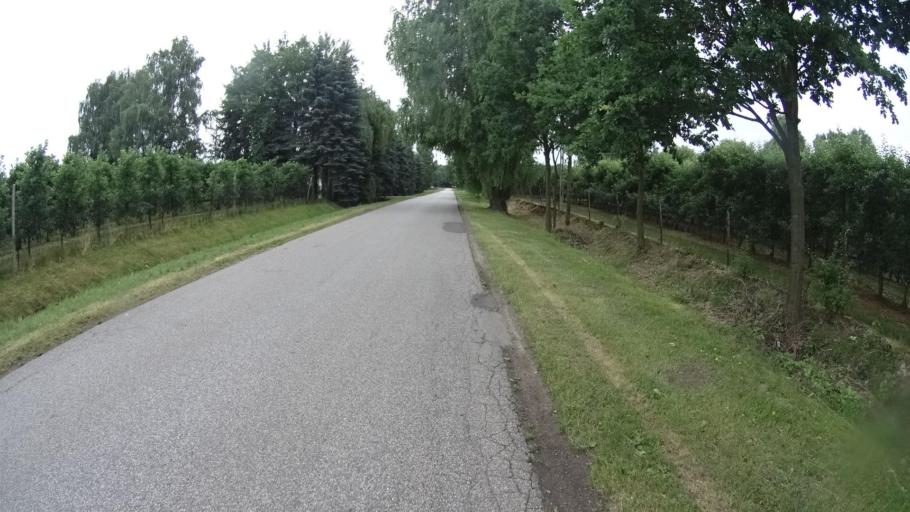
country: PL
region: Masovian Voivodeship
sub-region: Powiat grojecki
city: Goszczyn
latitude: 51.7861
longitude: 20.8552
